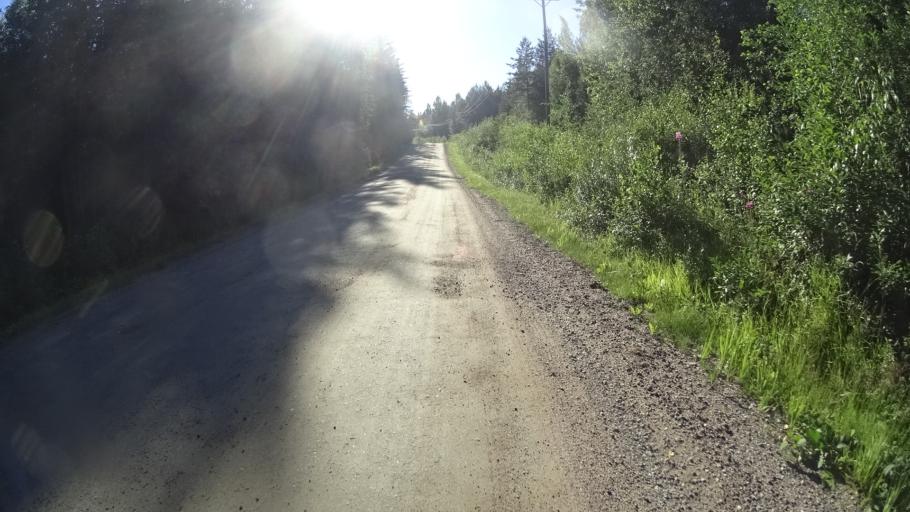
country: FI
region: Uusimaa
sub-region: Helsinki
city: Karkkila
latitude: 60.6480
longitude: 24.1371
